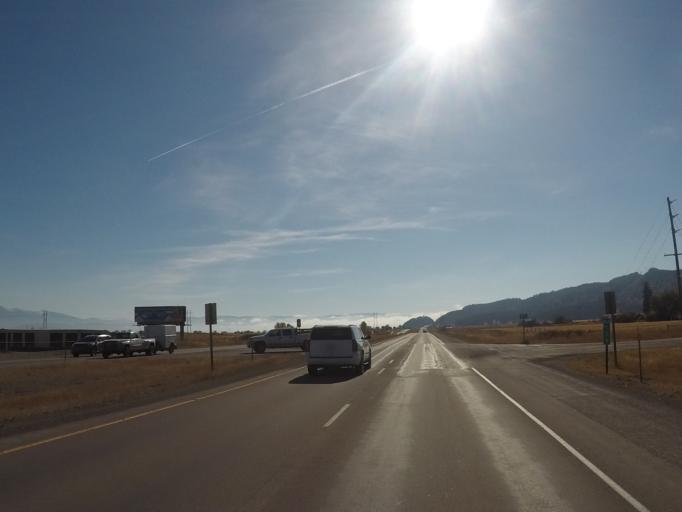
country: US
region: Montana
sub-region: Flathead County
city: Somers
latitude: 48.1177
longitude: -114.2559
